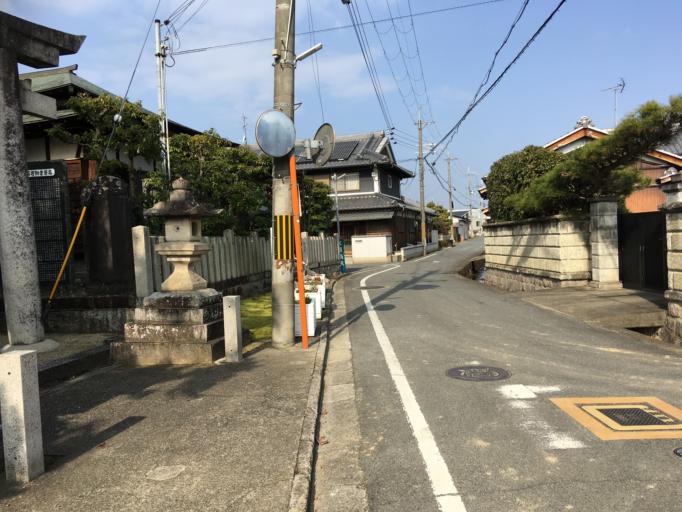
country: JP
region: Nara
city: Tawaramoto
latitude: 34.6090
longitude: 135.7834
